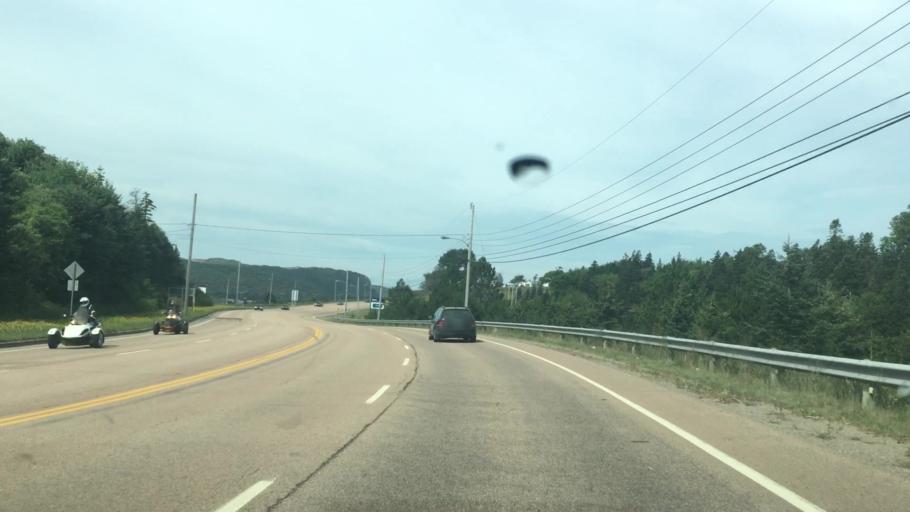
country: CA
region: Nova Scotia
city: Port Hawkesbury
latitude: 45.6250
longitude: -61.3667
